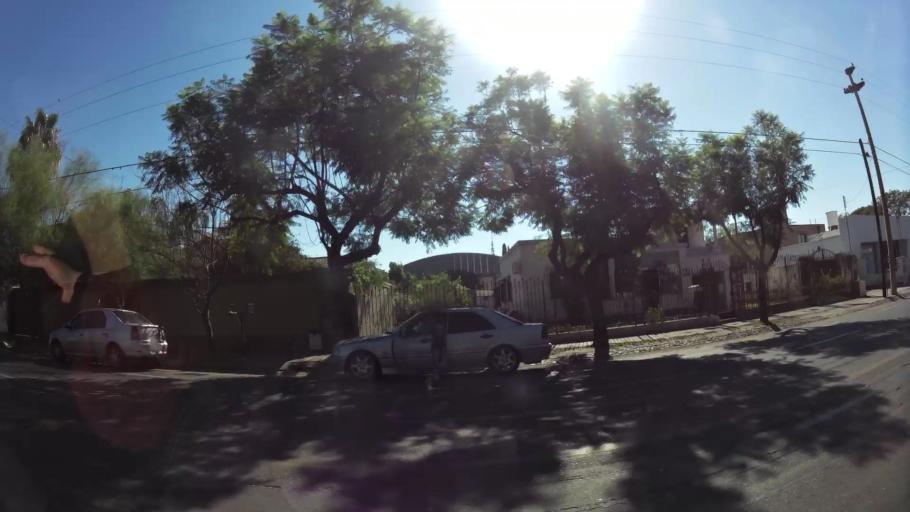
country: AR
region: Cordoba
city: Villa Allende
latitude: -31.3536
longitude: -64.2473
